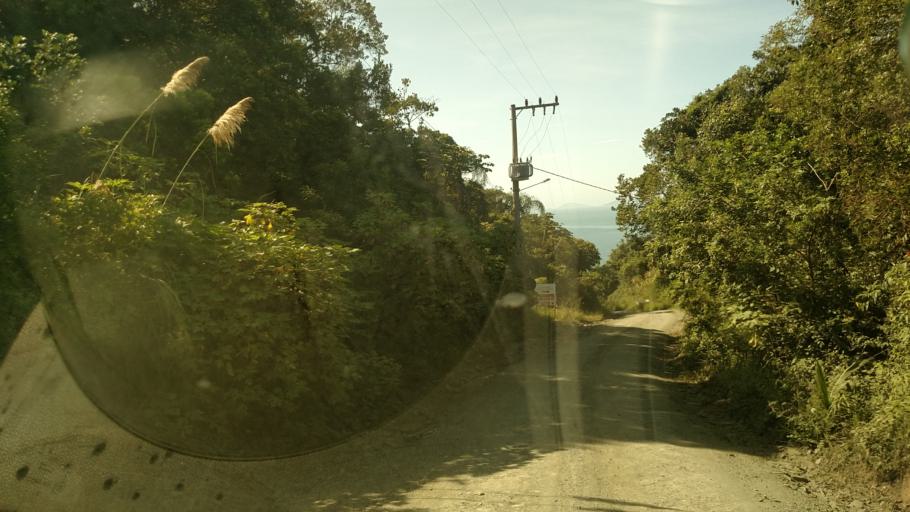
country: BR
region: Santa Catarina
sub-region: Porto Belo
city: Porto Belo
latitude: -27.2142
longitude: -48.5066
